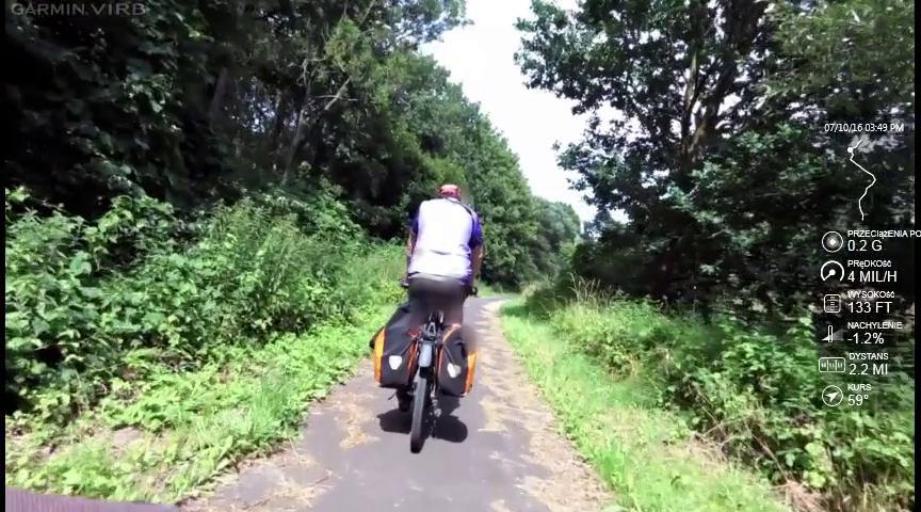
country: PL
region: West Pomeranian Voivodeship
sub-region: Powiat gryfinski
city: Banie
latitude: 53.1402
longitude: 14.6138
